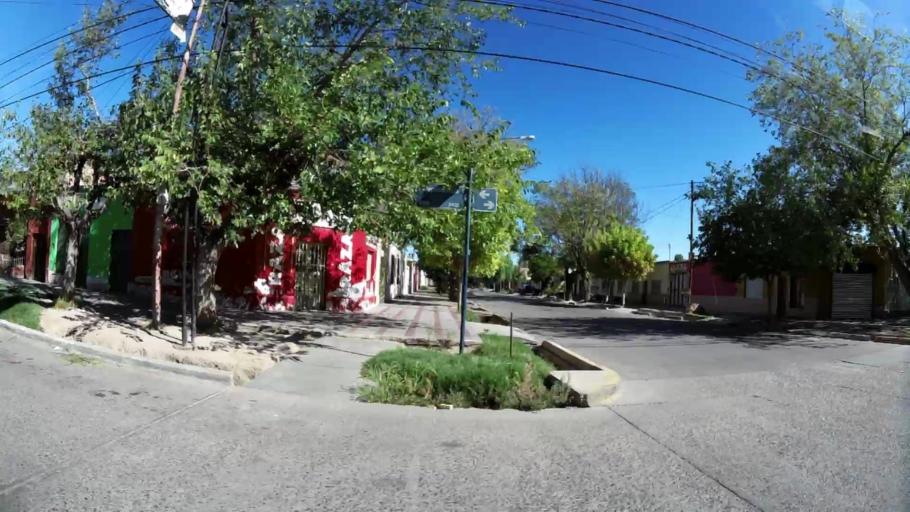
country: AR
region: Mendoza
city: Las Heras
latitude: -32.8424
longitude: -68.8077
